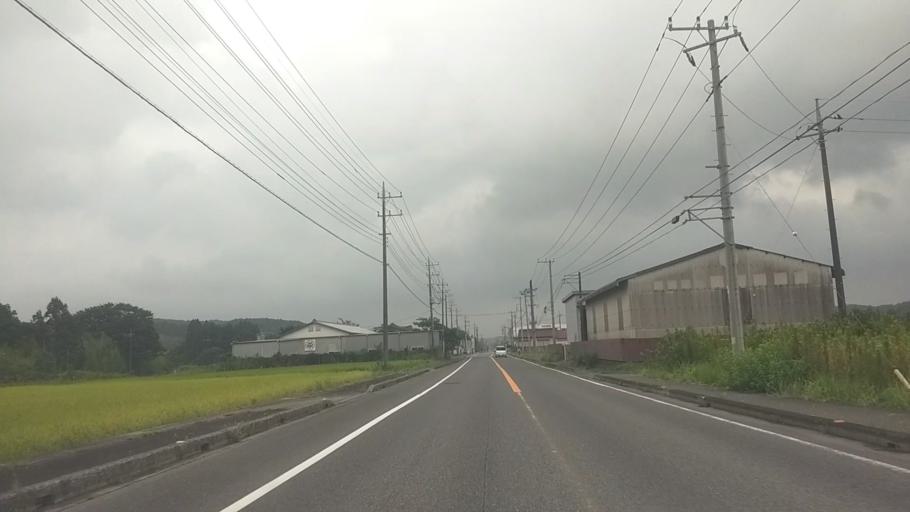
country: JP
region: Chiba
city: Ohara
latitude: 35.2870
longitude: 140.2609
